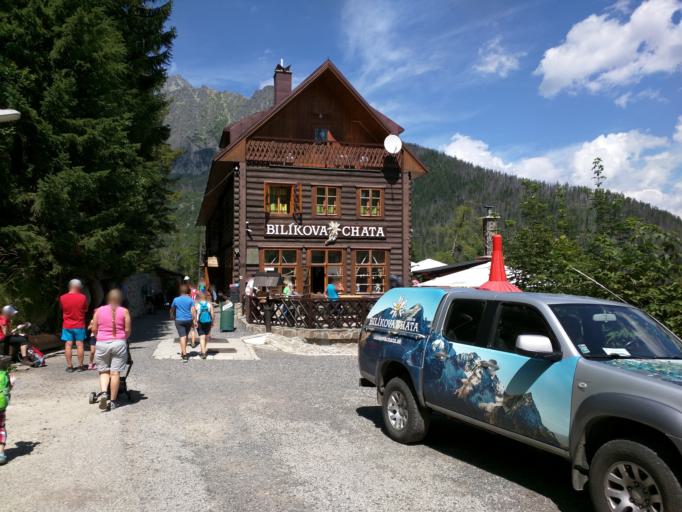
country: SK
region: Presovsky
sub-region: Okres Poprad
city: Vysoke Tatry
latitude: 49.1597
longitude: 20.2244
